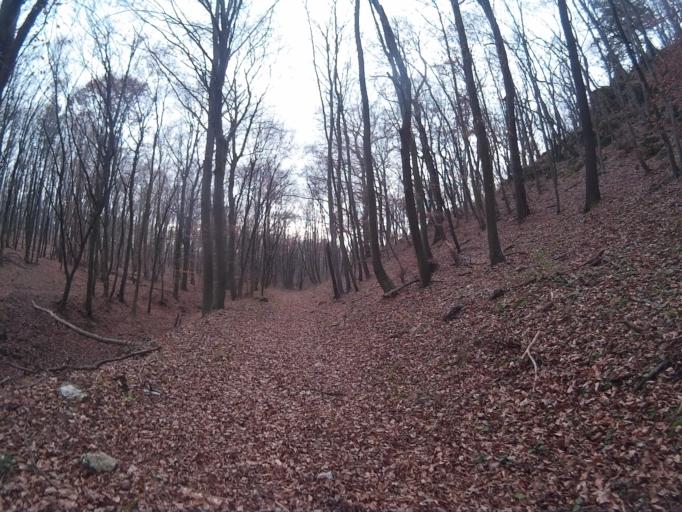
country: HU
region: Veszprem
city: Tapolca
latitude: 46.9449
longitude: 17.4942
